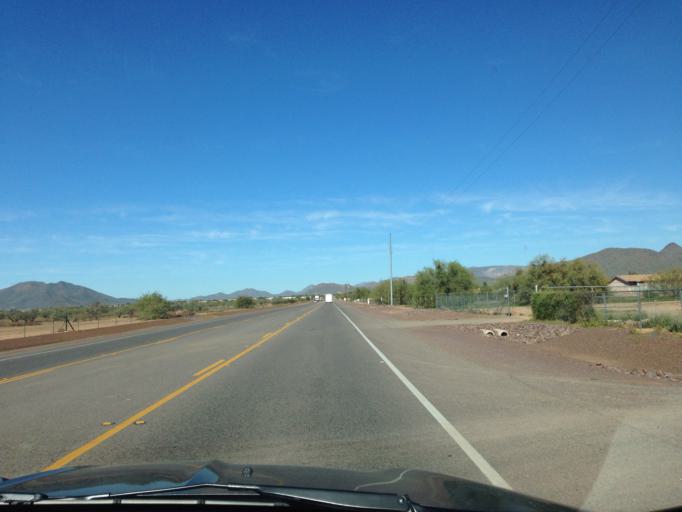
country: US
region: Arizona
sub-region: Maricopa County
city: Anthem
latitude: 33.8149
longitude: -112.0654
